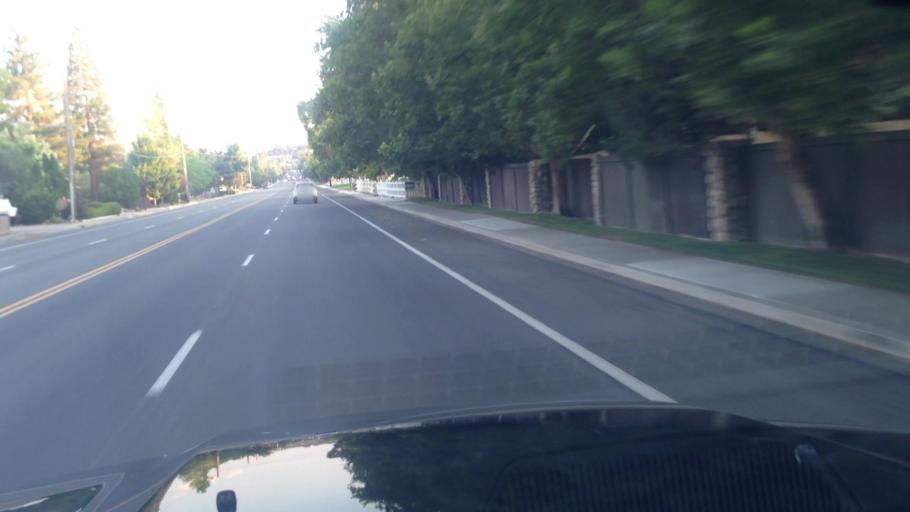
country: US
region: Nevada
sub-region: Washoe County
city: Reno
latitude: 39.4829
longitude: -119.8080
